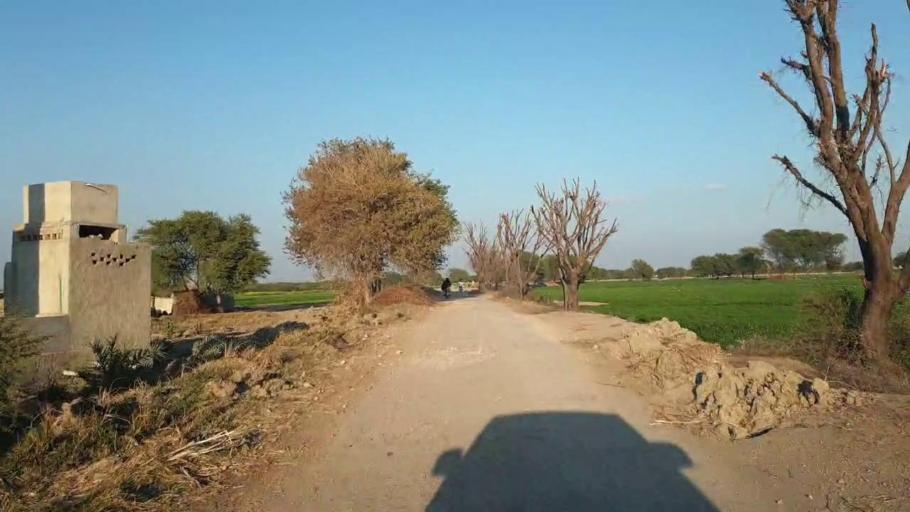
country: PK
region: Sindh
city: Shahpur Chakar
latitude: 26.1396
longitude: 68.5645
